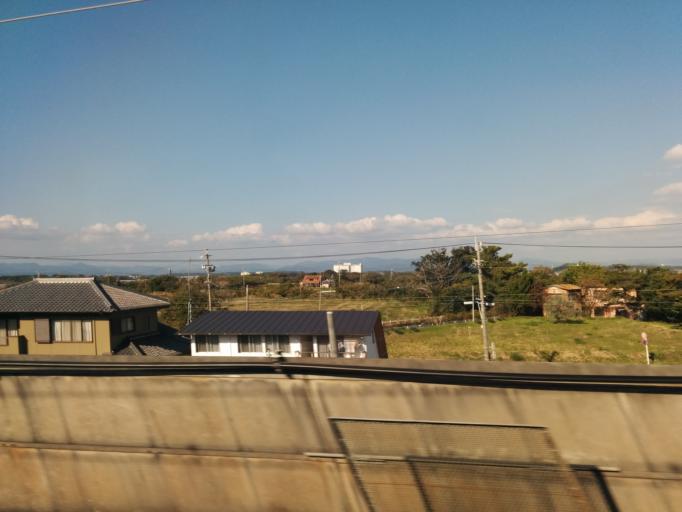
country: JP
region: Shizuoka
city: Kosai-shi
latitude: 34.6869
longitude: 137.6203
